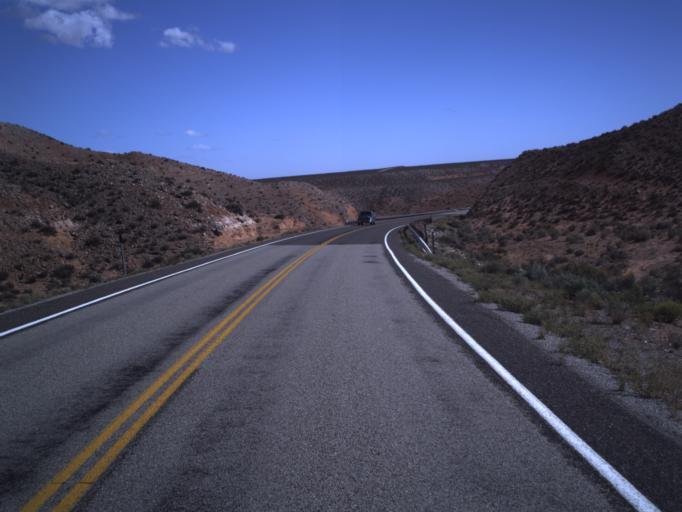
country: US
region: Utah
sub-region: Wayne County
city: Loa
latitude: 38.1441
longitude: -110.6122
